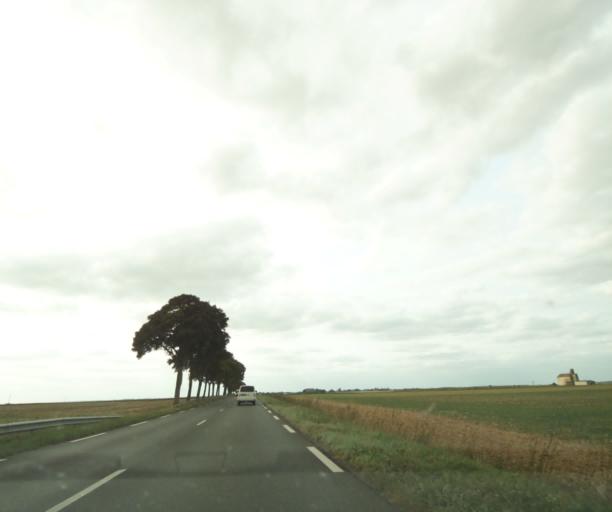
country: FR
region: Centre
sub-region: Departement d'Indre-et-Loire
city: Chambourg-sur-Indre
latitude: 47.1875
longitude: 0.9395
